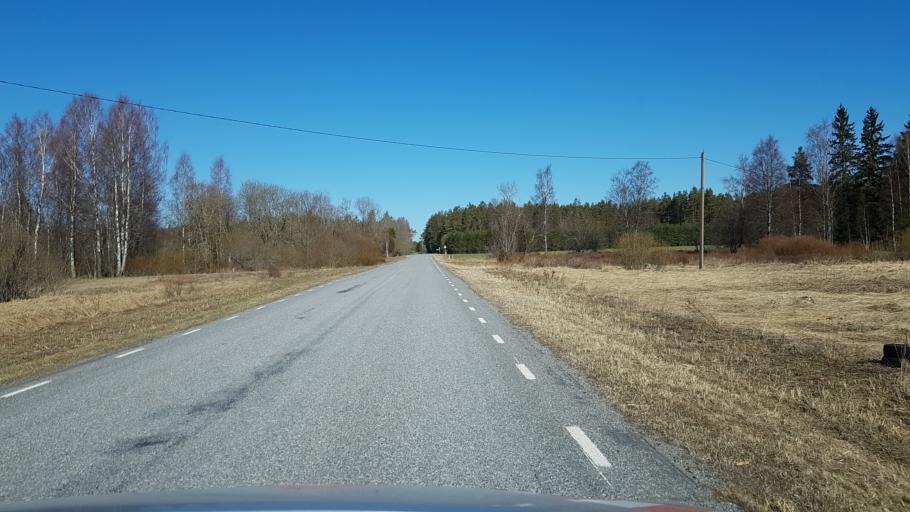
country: EE
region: Laeaene-Virumaa
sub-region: Haljala vald
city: Haljala
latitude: 59.4903
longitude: 26.2461
